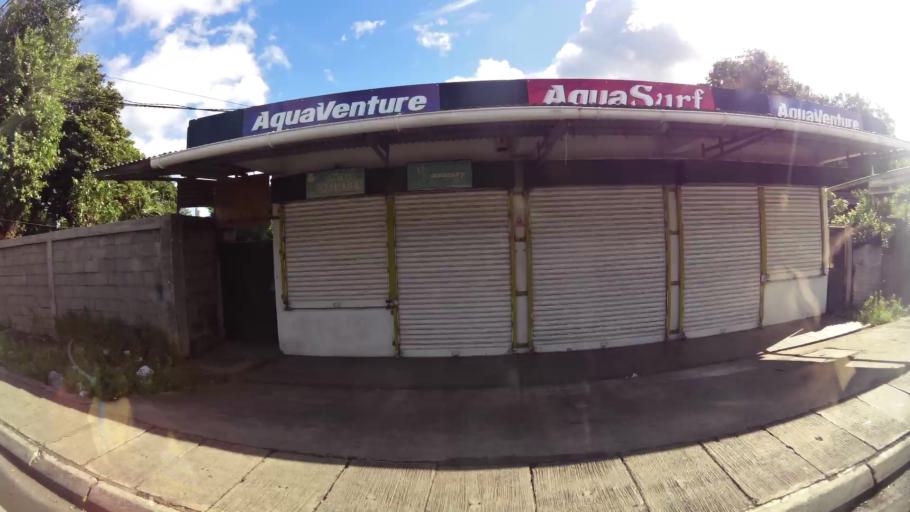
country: MU
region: Pamplemousses
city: Le Hochet
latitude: -20.1485
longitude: 57.5191
